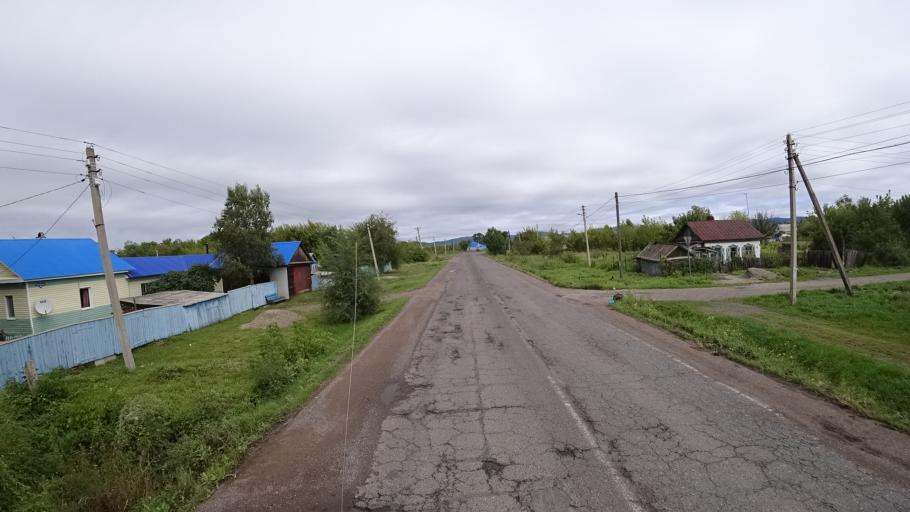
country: RU
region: Primorskiy
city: Monastyrishche
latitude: 44.2029
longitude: 132.4690
